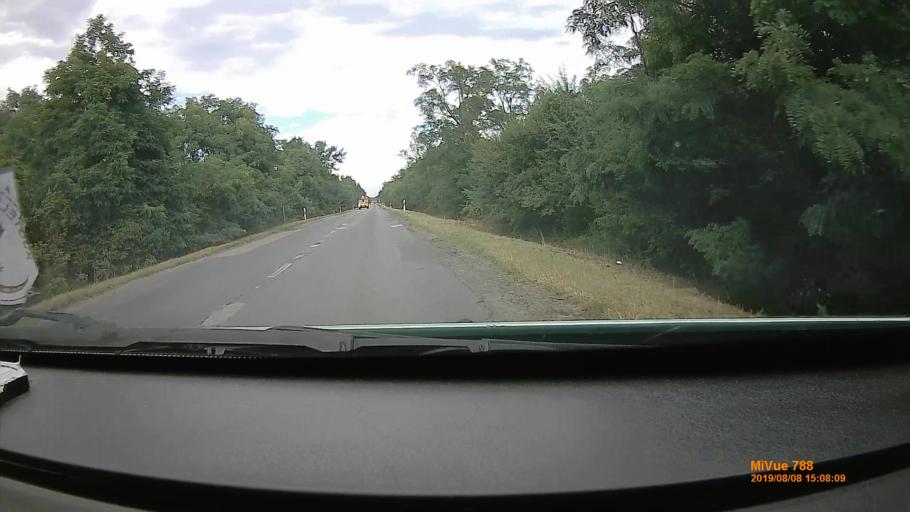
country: HU
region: Szabolcs-Szatmar-Bereg
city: Tunyogmatolcs
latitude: 47.9543
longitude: 22.4369
